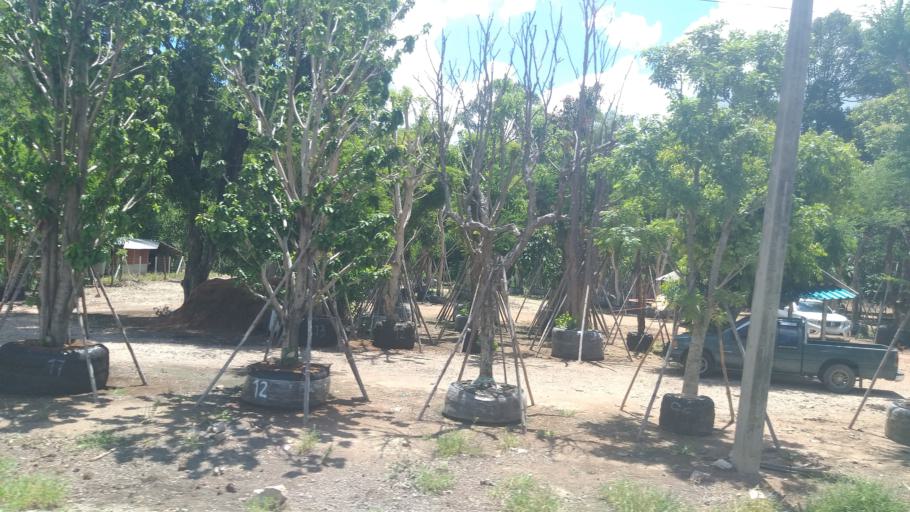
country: TH
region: Sara Buri
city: Wihan Daeng
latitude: 14.3859
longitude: 101.0944
